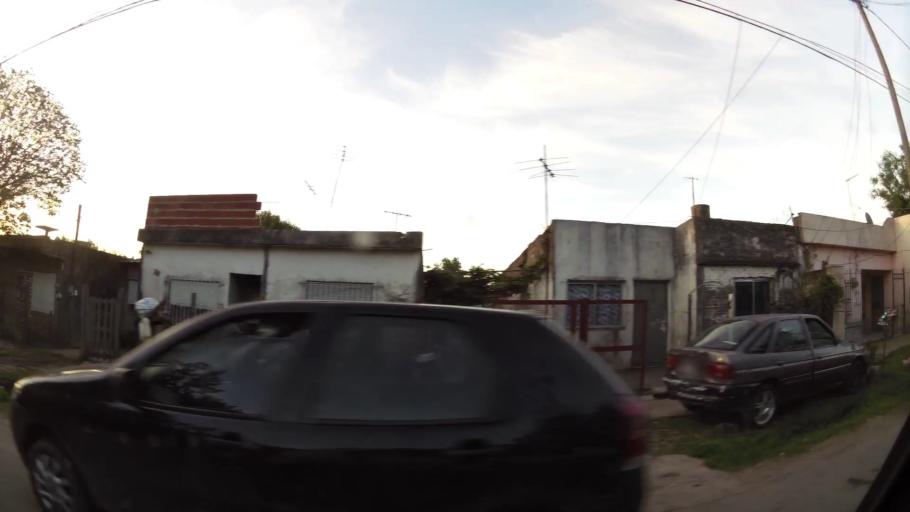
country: AR
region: Buenos Aires
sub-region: Partido de Quilmes
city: Quilmes
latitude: -34.7895
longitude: -58.2223
